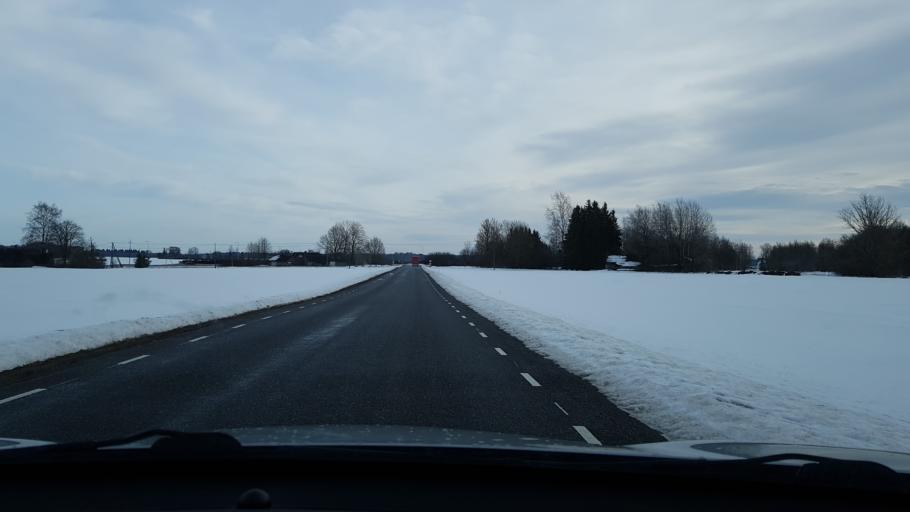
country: EE
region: Jaervamaa
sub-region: Paide linn
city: Paide
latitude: 58.8778
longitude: 25.6874
